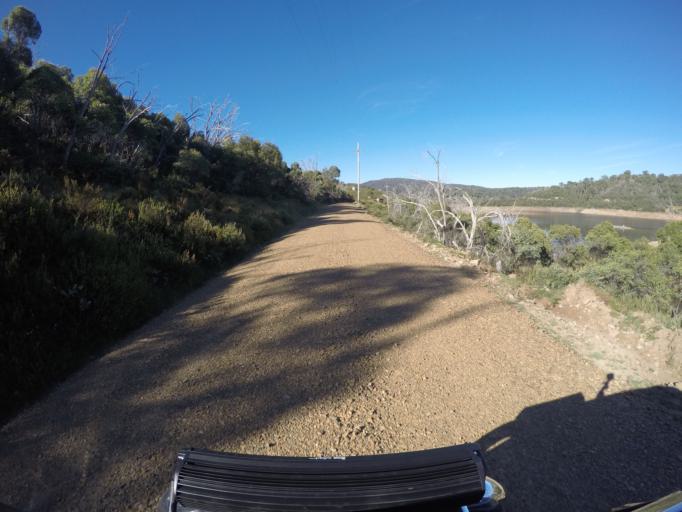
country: AU
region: New South Wales
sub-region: Snowy River
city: Jindabyne
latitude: -36.0526
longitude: 148.2805
